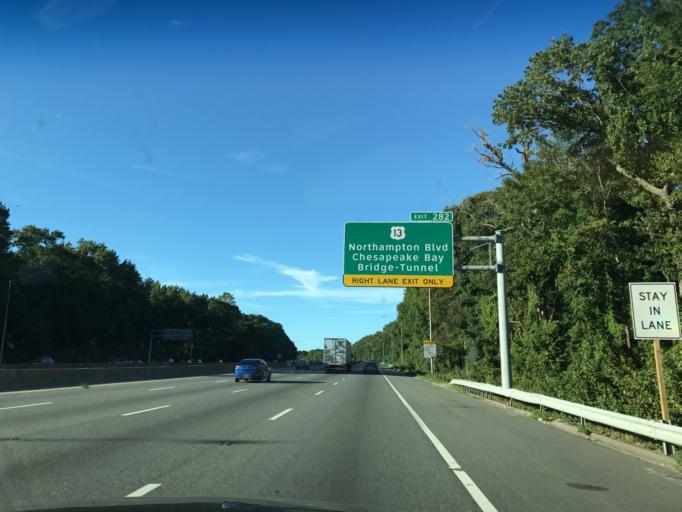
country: US
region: Virginia
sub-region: City of Norfolk
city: Norfolk
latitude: 36.8651
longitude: -76.1949
